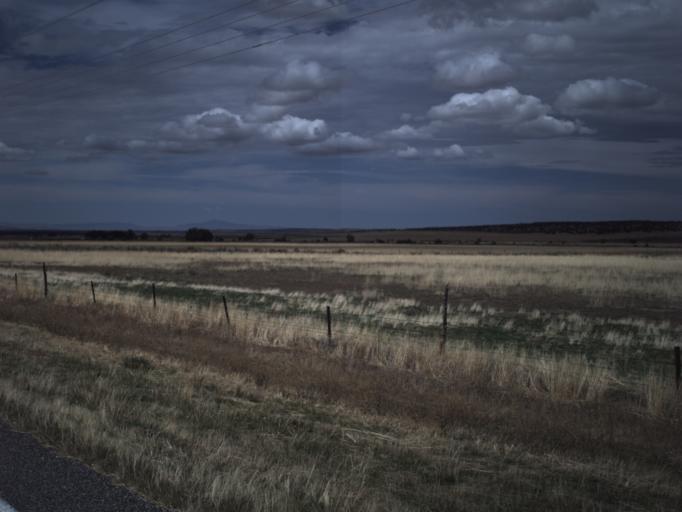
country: US
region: Utah
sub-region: Millard County
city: Fillmore
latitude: 38.9791
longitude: -112.3797
